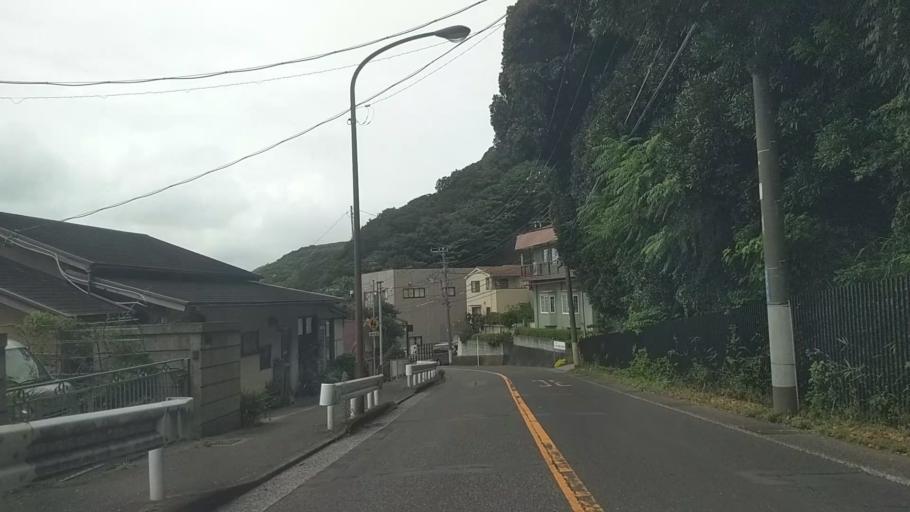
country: JP
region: Kanagawa
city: Yokosuka
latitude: 35.2575
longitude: 139.7191
